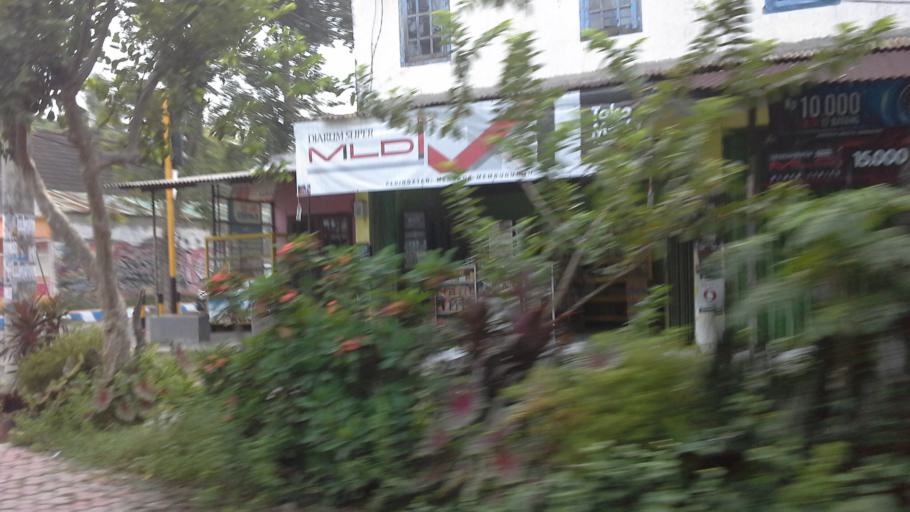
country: ID
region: East Java
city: Bondowoso
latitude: -7.9250
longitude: 113.8264
